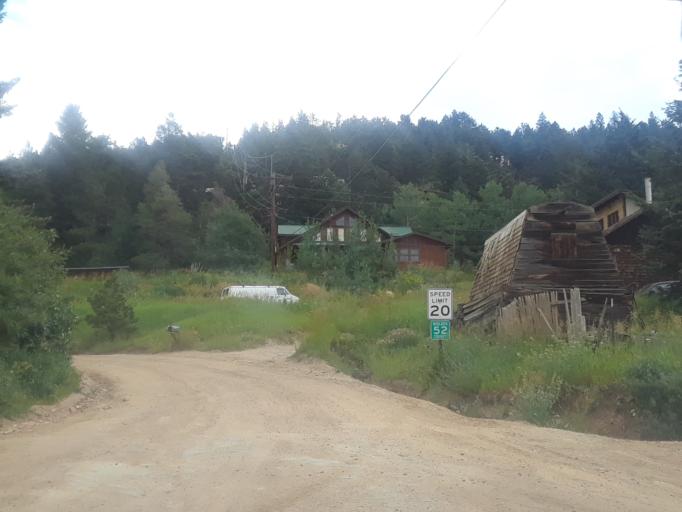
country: US
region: Colorado
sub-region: Boulder County
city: Nederland
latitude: 40.0634
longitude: -105.4083
